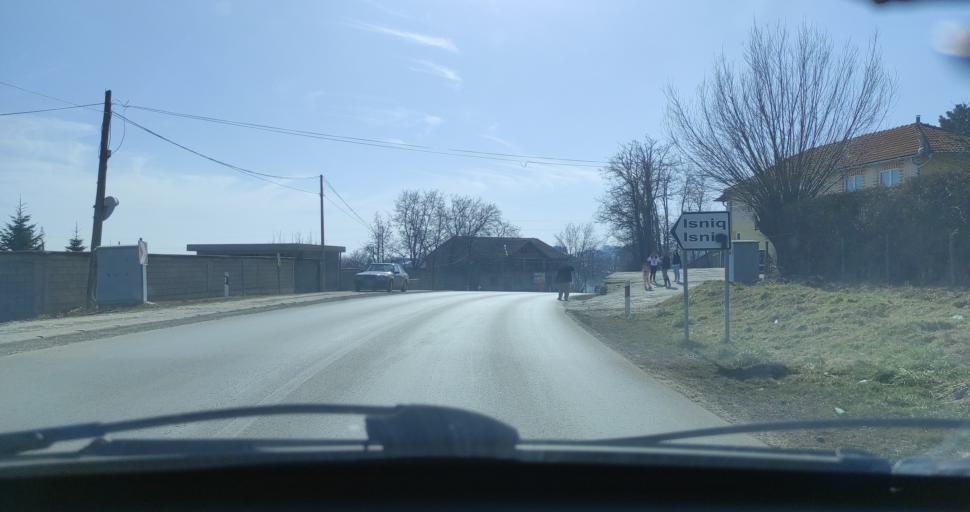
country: XK
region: Gjakova
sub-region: Komuna e Decanit
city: Lebushe
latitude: 42.5521
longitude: 20.2911
